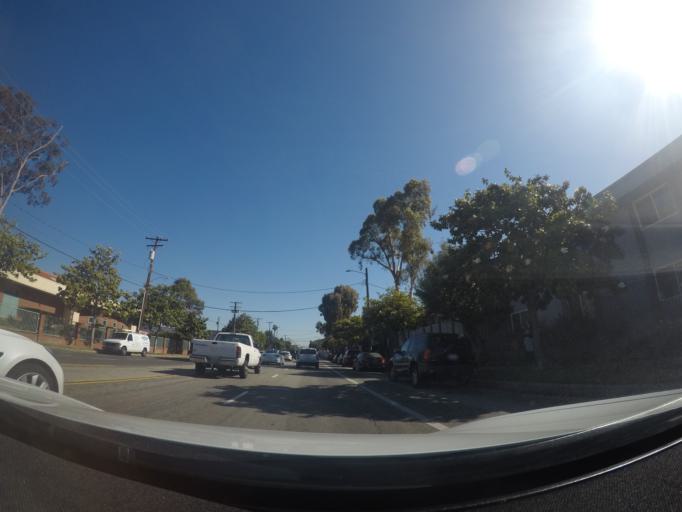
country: US
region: California
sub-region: Los Angeles County
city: Torrance
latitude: 33.8436
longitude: -118.3623
